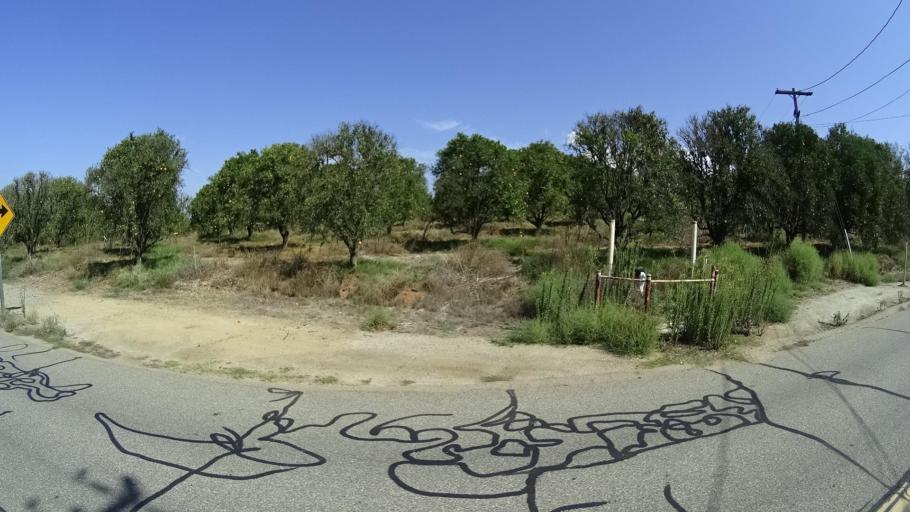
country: US
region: California
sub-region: San Diego County
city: Valley Center
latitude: 33.2819
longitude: -117.0269
